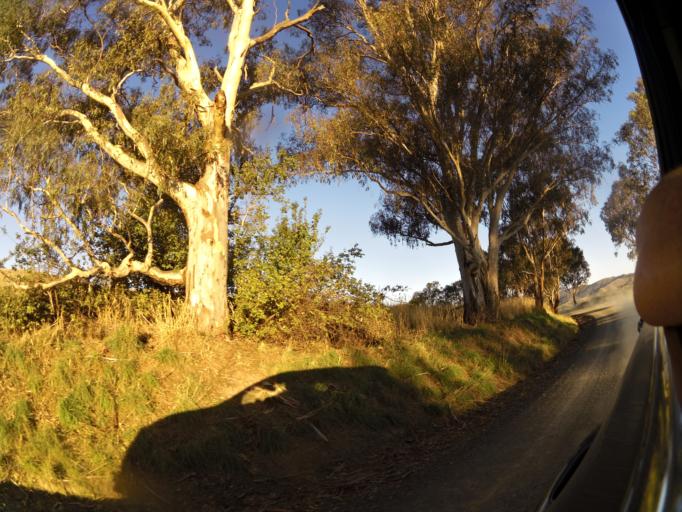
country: AU
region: Victoria
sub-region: Murrindindi
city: Alexandra
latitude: -37.1538
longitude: 145.5338
